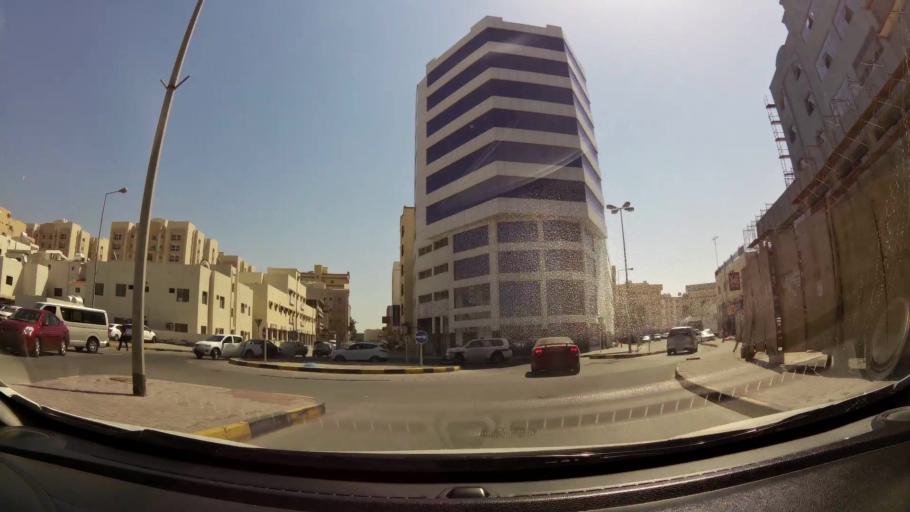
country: BH
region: Manama
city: Manama
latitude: 26.2039
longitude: 50.5965
